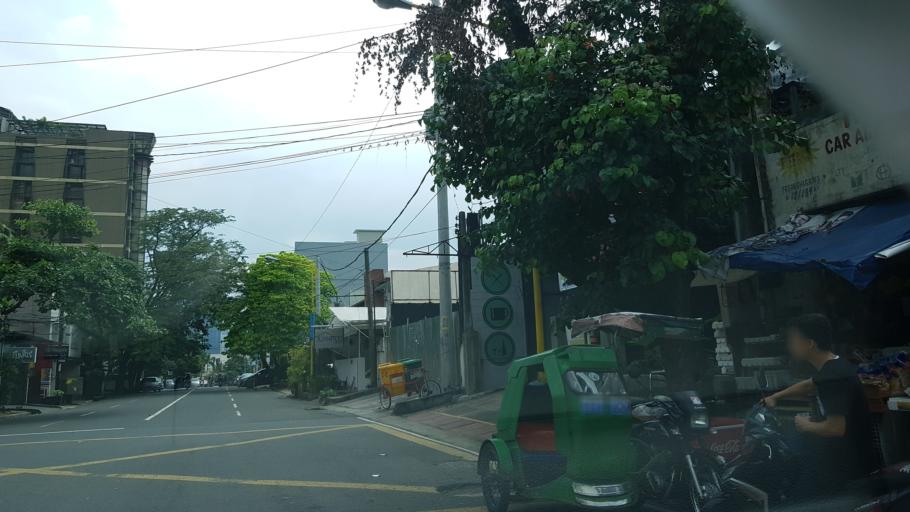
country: PH
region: Metro Manila
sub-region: Pasig
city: Pasig City
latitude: 14.5694
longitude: 121.0603
